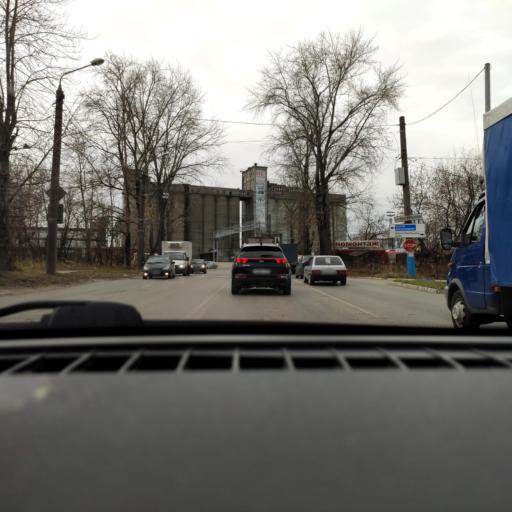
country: RU
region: Perm
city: Froly
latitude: 57.9546
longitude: 56.2412
